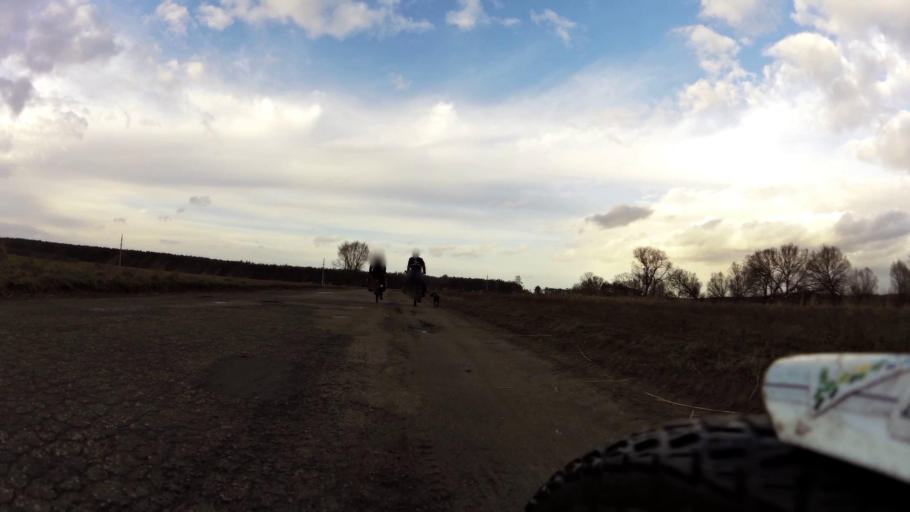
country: PL
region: West Pomeranian Voivodeship
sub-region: Powiat kamienski
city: Kamien Pomorski
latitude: 53.9009
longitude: 14.7318
